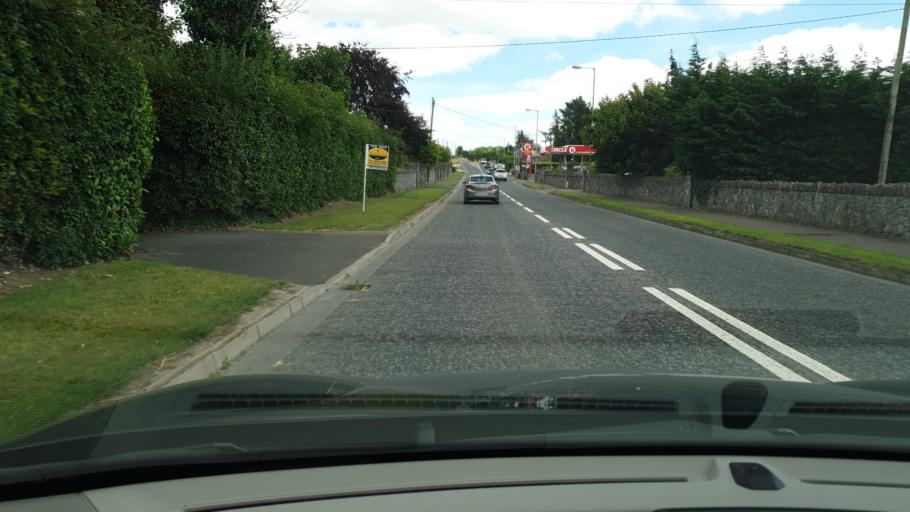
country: IE
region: Leinster
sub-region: An Mhi
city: Newtown Trim
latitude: 53.5264
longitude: -6.6738
